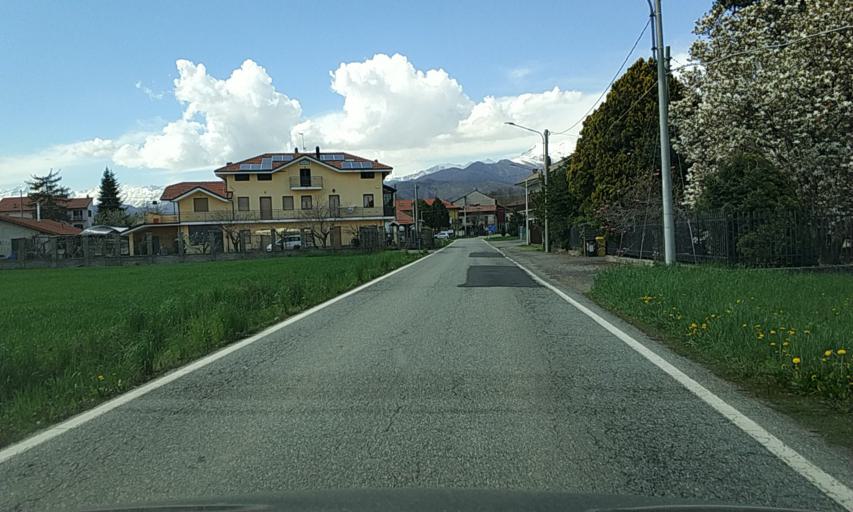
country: IT
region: Piedmont
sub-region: Provincia di Torino
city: Nole
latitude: 45.2562
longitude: 7.5842
